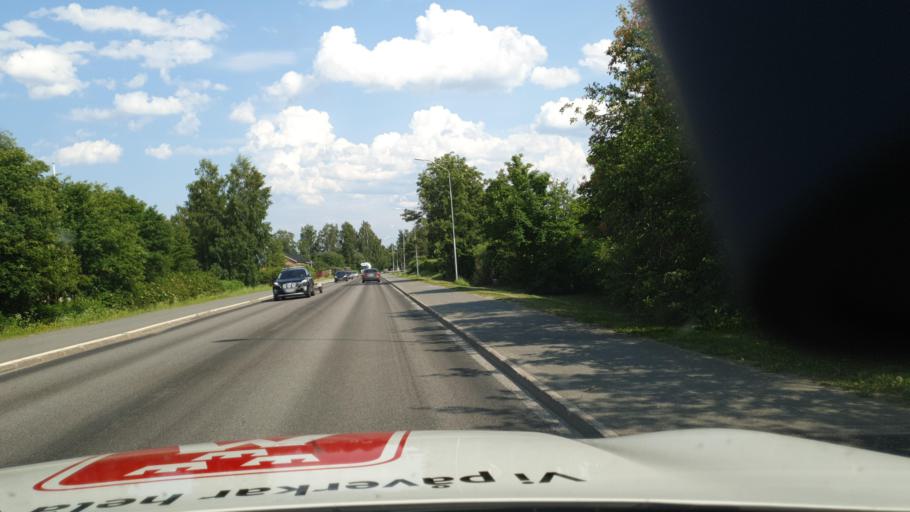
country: SE
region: Vaesterbotten
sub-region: Skelleftea Kommun
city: Viken
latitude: 64.7466
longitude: 20.9208
